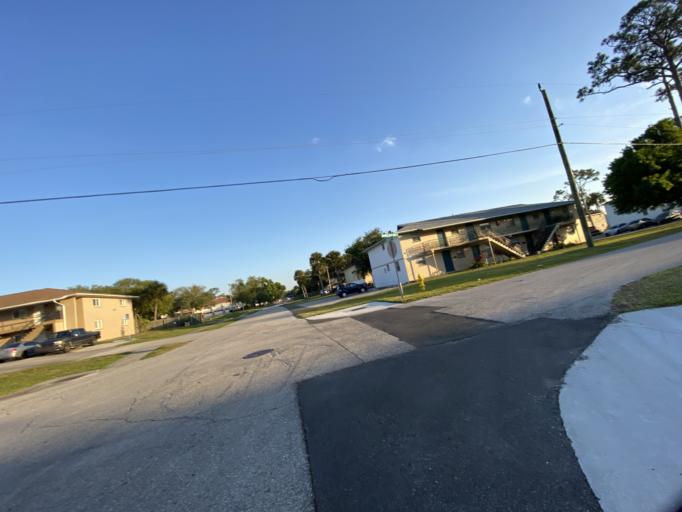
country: US
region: Florida
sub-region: Volusia County
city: South Daytona
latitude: 29.1818
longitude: -81.0092
